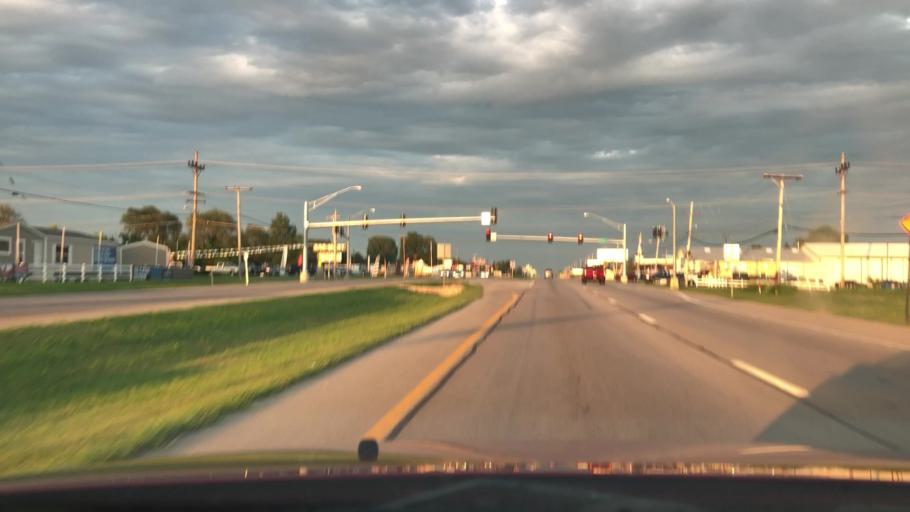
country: US
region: Missouri
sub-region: Greene County
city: Springfield
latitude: 37.1829
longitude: -93.3465
